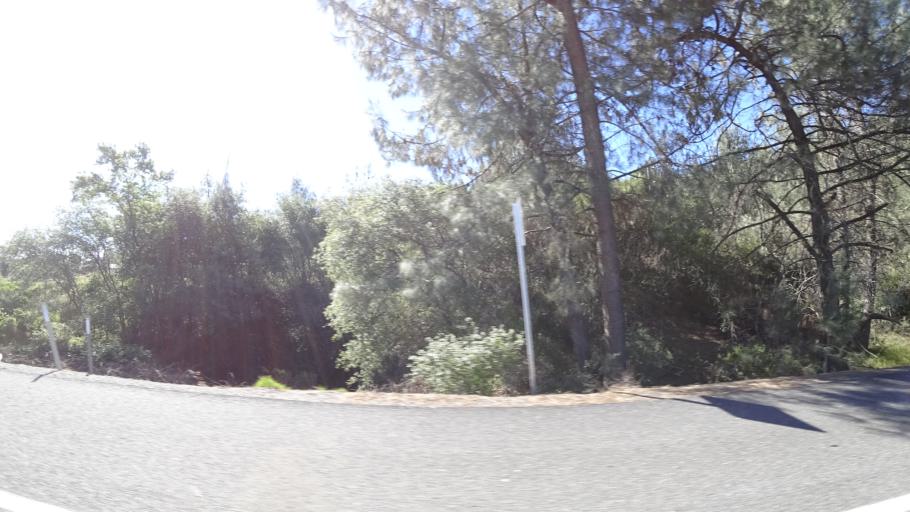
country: US
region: California
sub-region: Placer County
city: Newcastle
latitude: 38.8773
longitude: -121.1242
